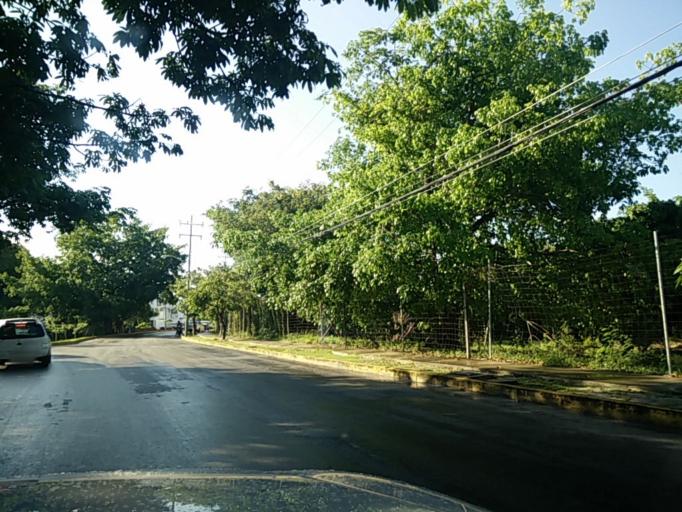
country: MX
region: Quintana Roo
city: Cancun
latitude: 21.1477
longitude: -86.8294
